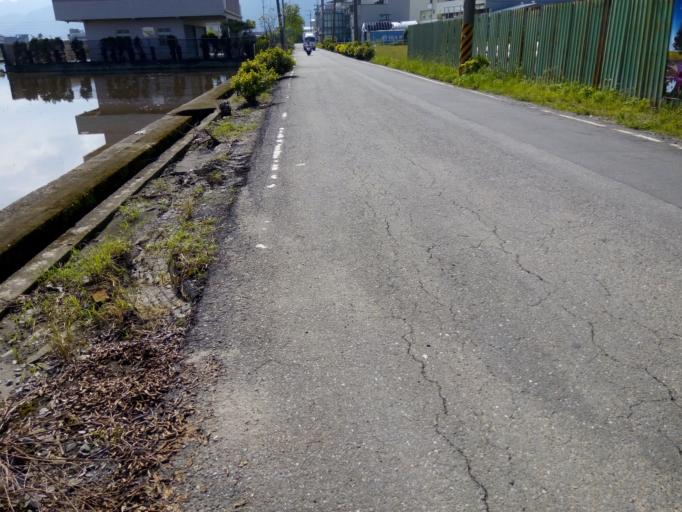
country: TW
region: Taiwan
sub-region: Yilan
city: Yilan
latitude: 24.6714
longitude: 121.7788
